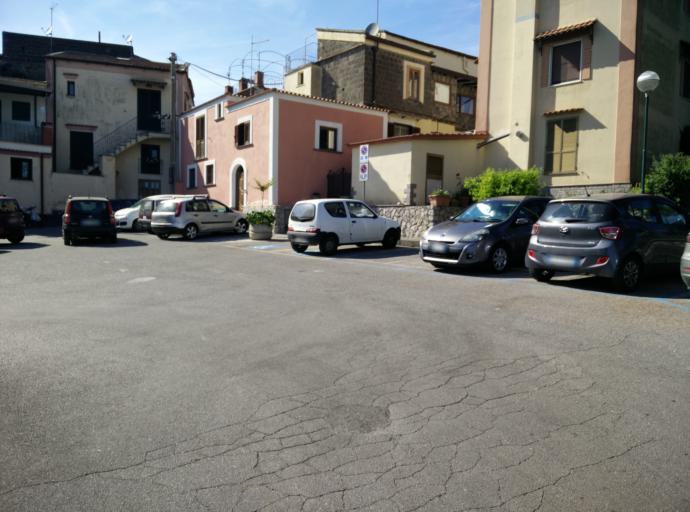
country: IT
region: Campania
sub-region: Provincia di Napoli
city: Massa Lubrense
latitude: 40.6001
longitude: 14.3846
